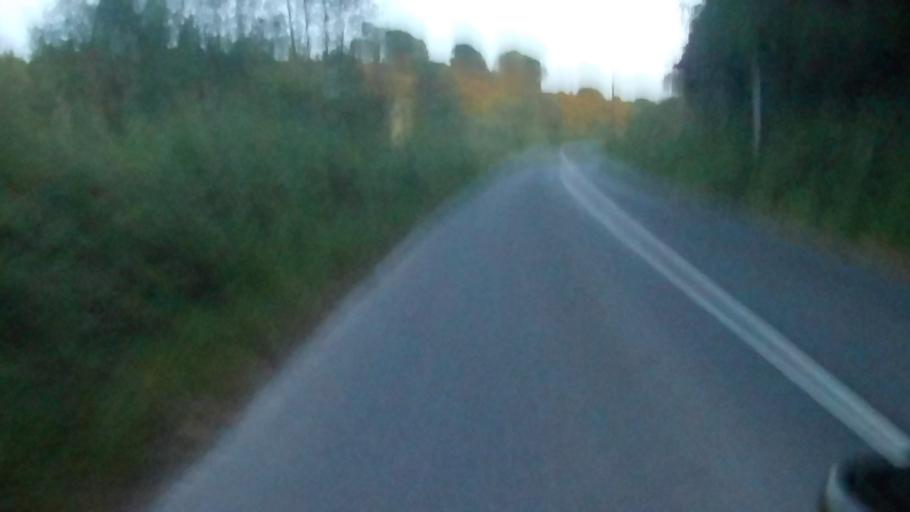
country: IE
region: Munster
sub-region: County Cork
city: Carrigtwohill
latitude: 51.9404
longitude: -8.3151
